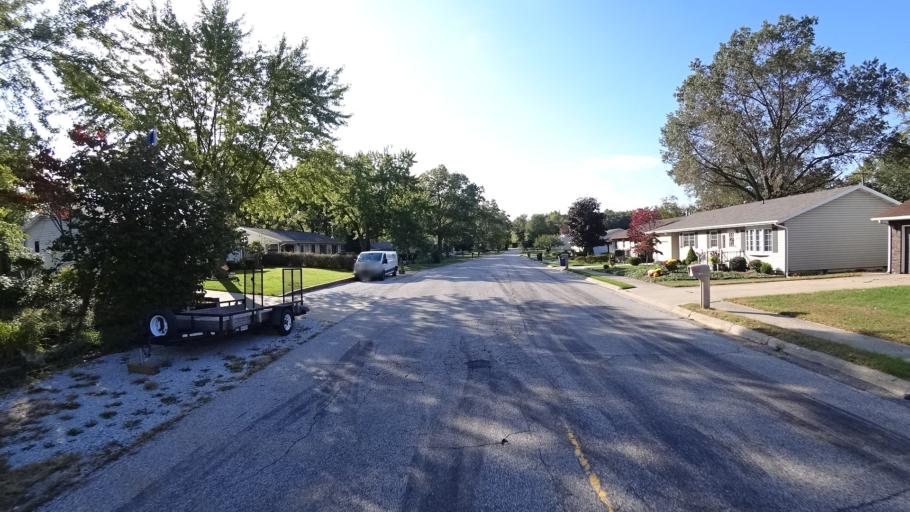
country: US
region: Indiana
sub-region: LaPorte County
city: Trail Creek
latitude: 41.7007
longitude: -86.8647
